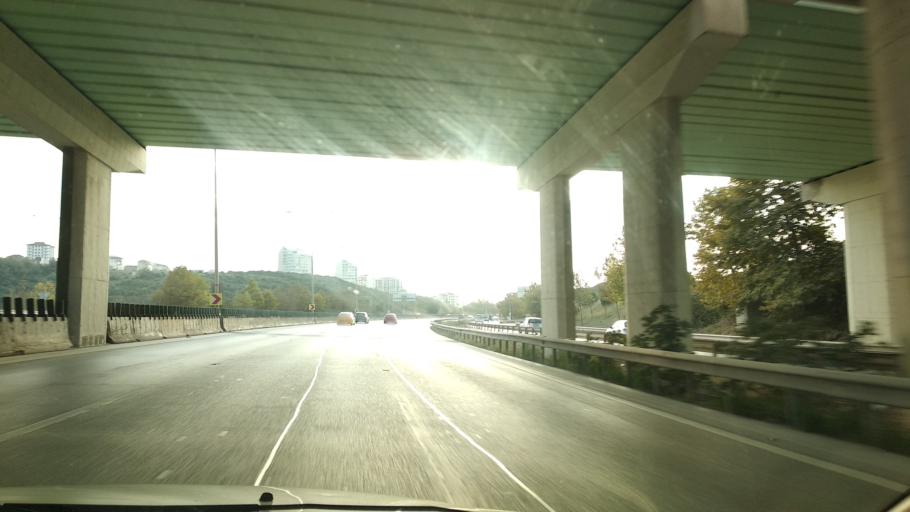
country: TR
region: Istanbul
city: Icmeler
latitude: 40.8789
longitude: 29.3140
